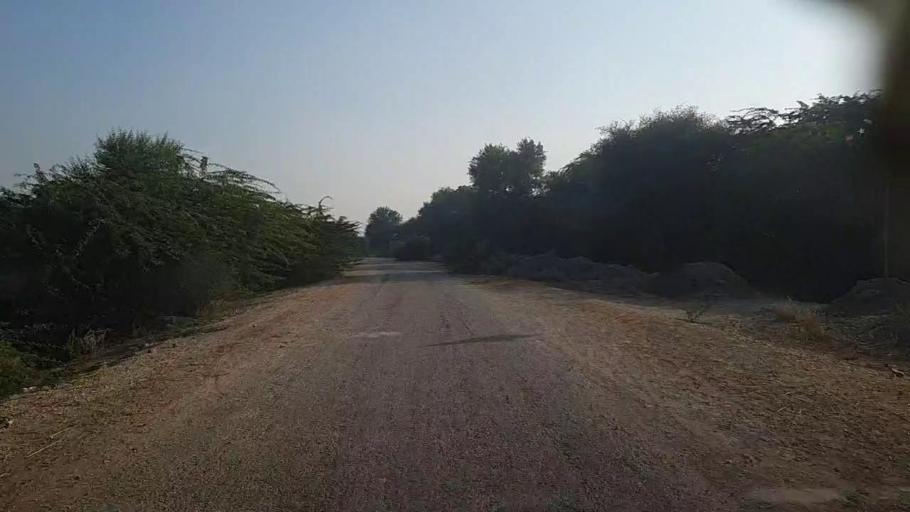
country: PK
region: Sindh
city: Karaundi
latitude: 26.7428
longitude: 68.4770
